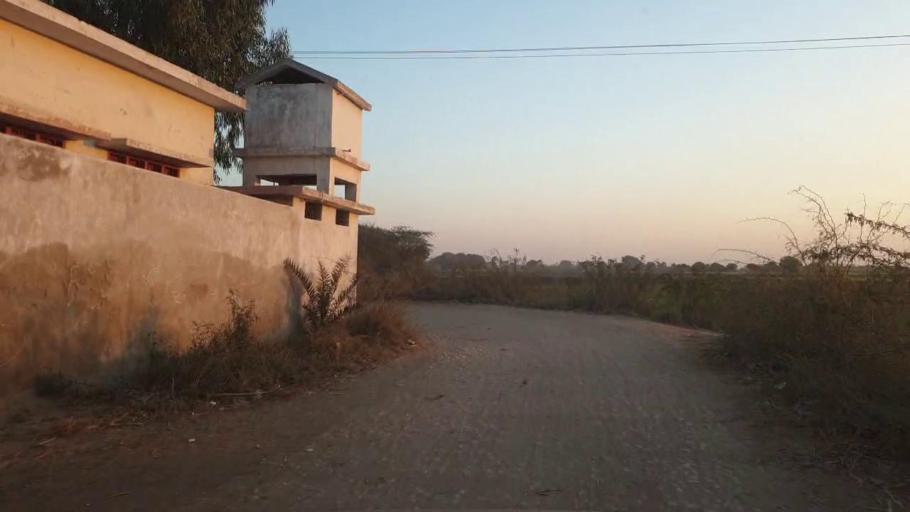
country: PK
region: Sindh
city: Chambar
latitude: 25.3546
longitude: 68.7494
